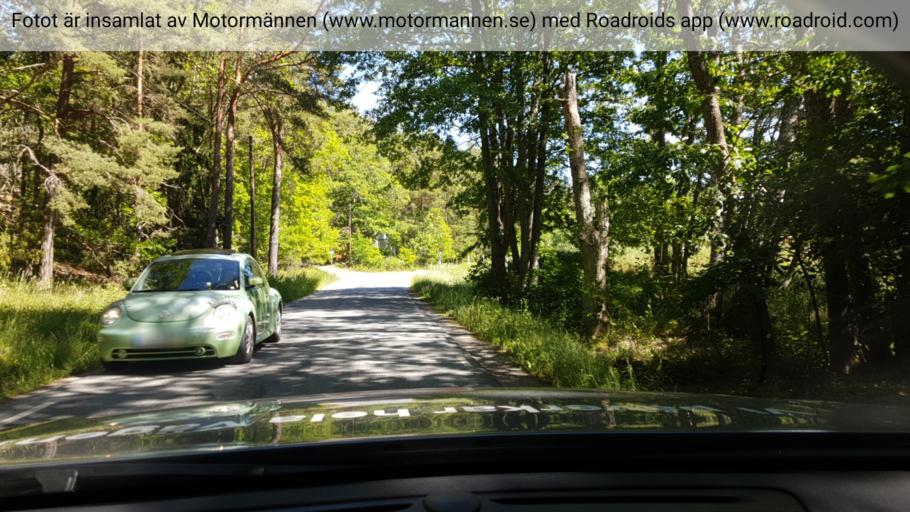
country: SE
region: Stockholm
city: Dalaro
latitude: 59.1592
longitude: 18.4406
